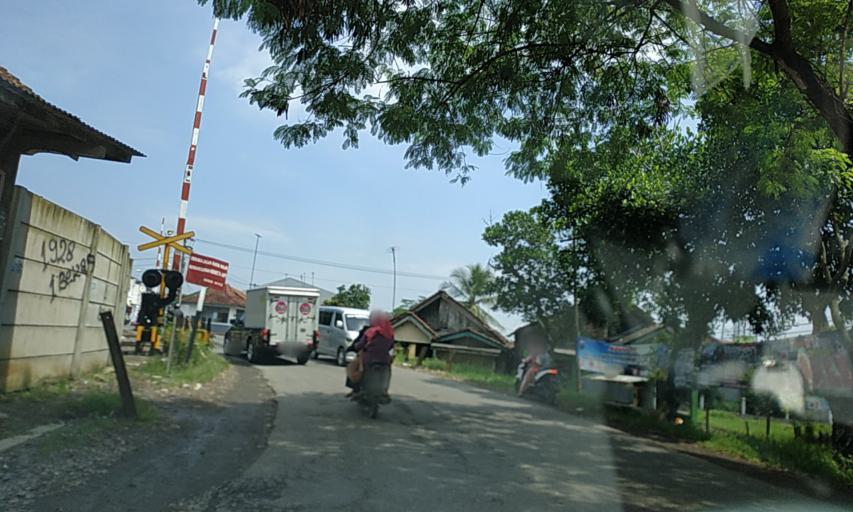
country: ID
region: Central Java
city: Sidamulya
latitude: -7.4858
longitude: 108.8067
